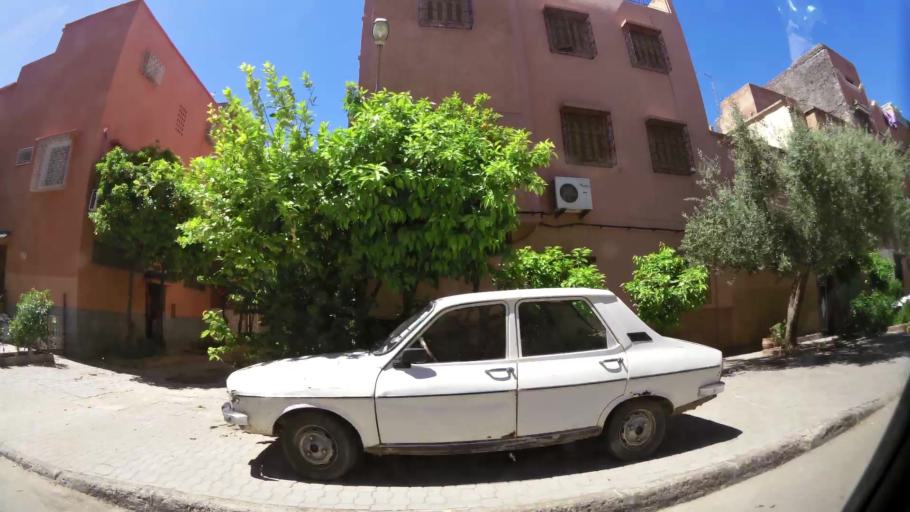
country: MA
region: Marrakech-Tensift-Al Haouz
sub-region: Marrakech
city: Marrakesh
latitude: 31.6472
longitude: -7.9959
